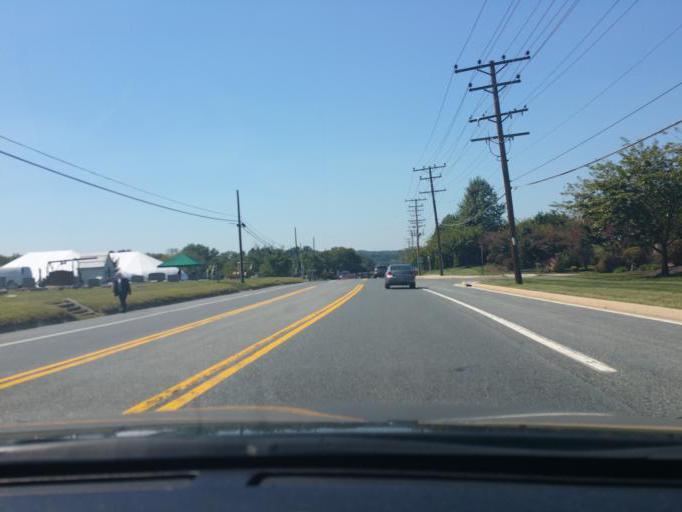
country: US
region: Maryland
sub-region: Harford County
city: South Bel Air
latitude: 39.5480
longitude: -76.3085
